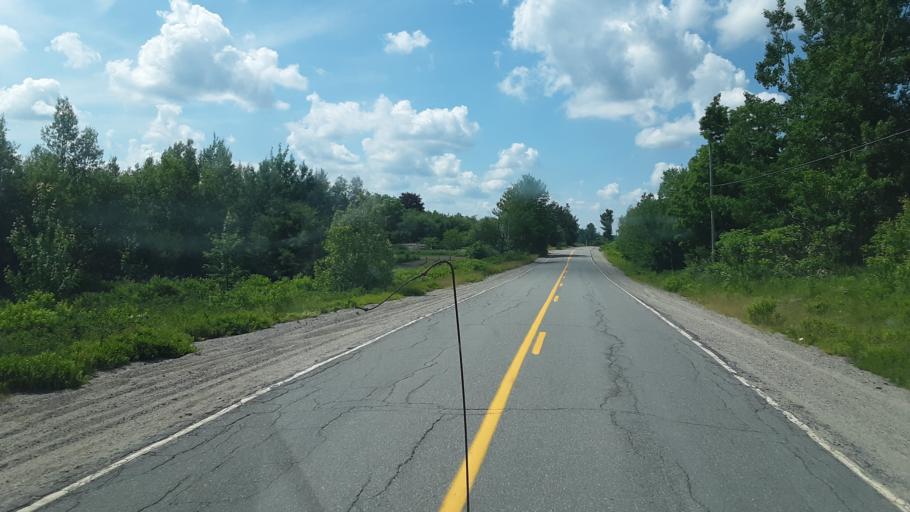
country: US
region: Maine
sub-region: Washington County
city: Machias
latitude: 44.9228
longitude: -67.6569
